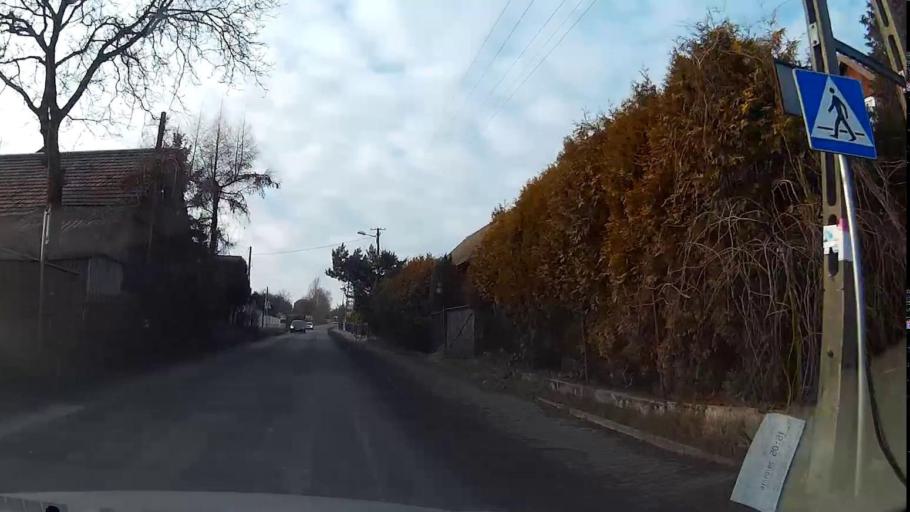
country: PL
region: Lesser Poland Voivodeship
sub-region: Powiat krakowski
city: Czulow
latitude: 50.0615
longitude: 19.6915
